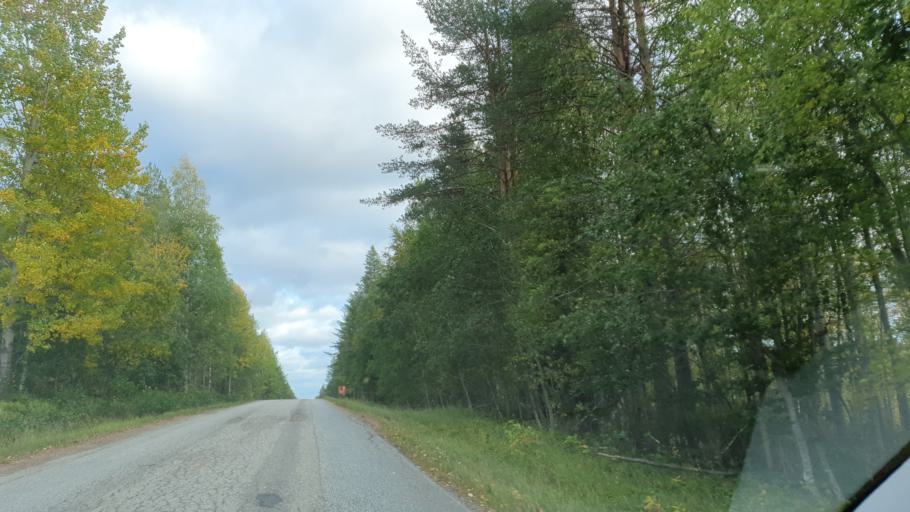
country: FI
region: North Karelia
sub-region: Pielisen Karjala
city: Lieksa
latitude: 63.9132
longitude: 30.1902
